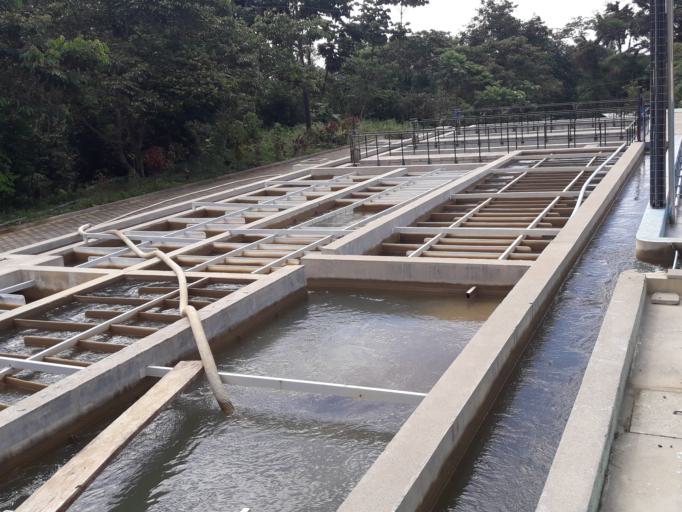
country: EC
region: Napo
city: Archidona
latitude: -0.9459
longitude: -77.8913
